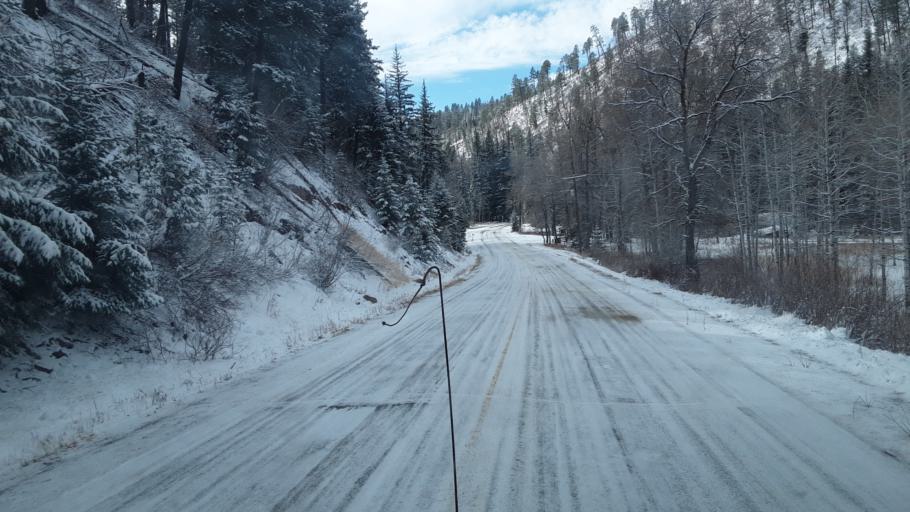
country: US
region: Colorado
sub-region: La Plata County
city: Bayfield
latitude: 37.3726
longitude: -107.6625
